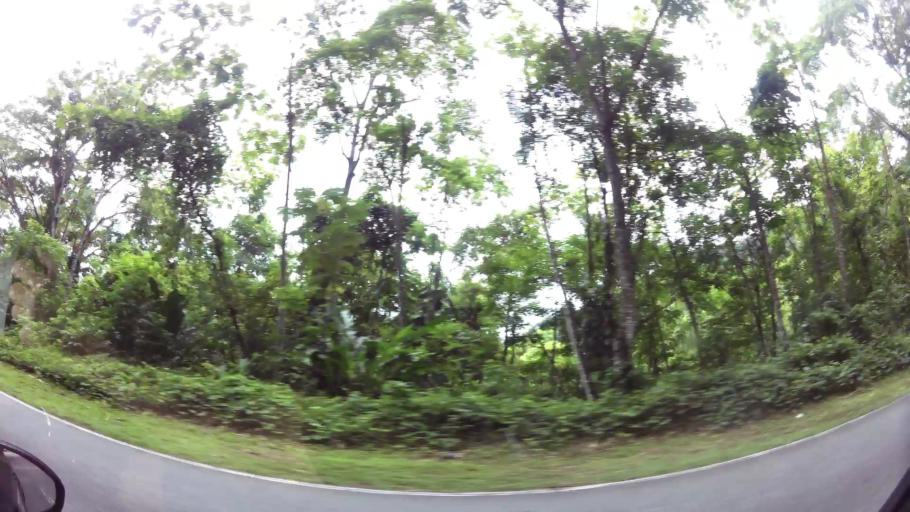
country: TT
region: Diego Martin
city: Petit Valley
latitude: 10.7441
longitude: -61.4930
